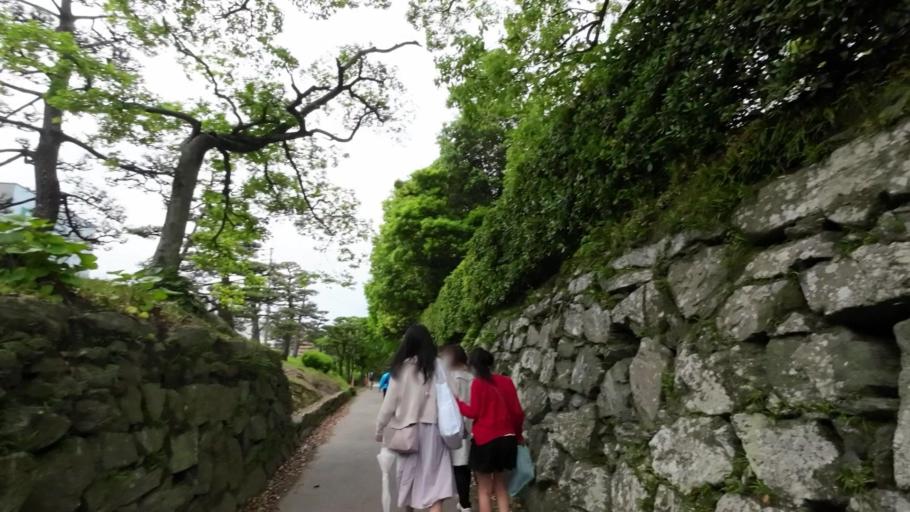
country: JP
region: Tokushima
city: Tokushima-shi
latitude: 34.0738
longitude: 134.5568
